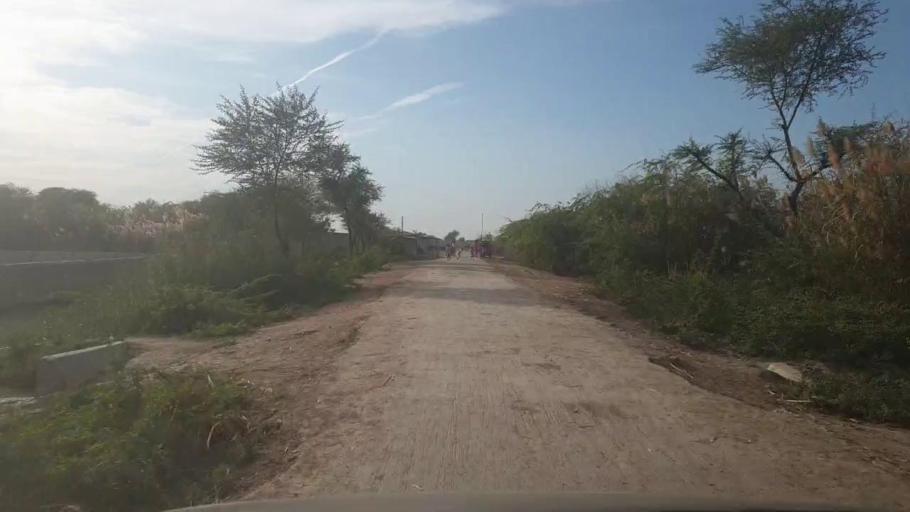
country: PK
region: Sindh
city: Samaro
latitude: 25.3344
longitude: 69.2377
